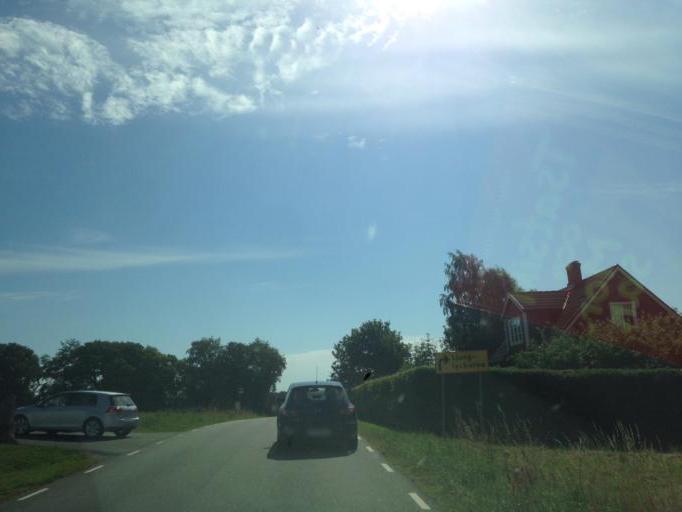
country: SE
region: Skane
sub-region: Simrishamns Kommun
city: Kivik
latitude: 55.6351
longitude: 14.1557
